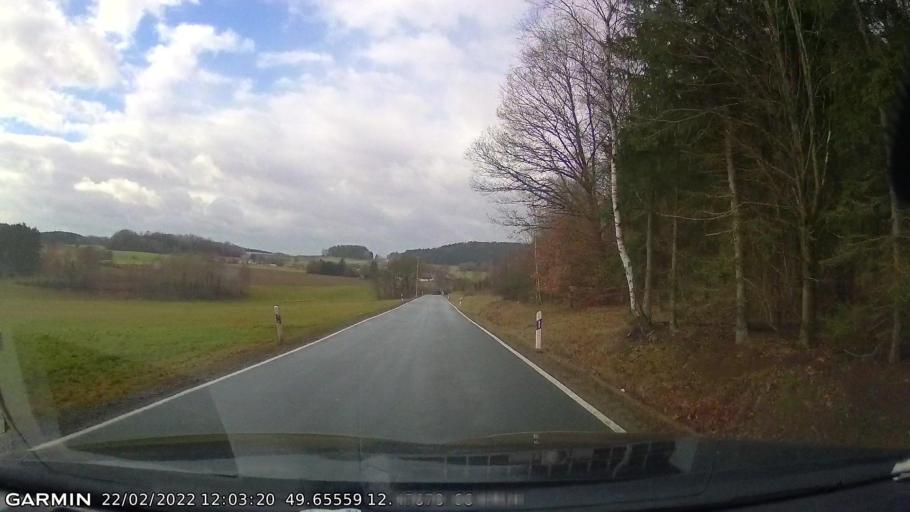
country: DE
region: Bavaria
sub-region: Upper Palatinate
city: Waidhaus
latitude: 49.6556
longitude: 12.4767
